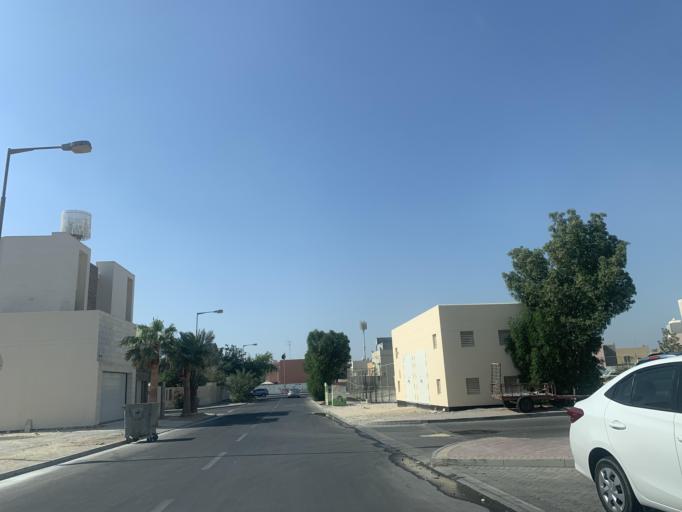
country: BH
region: Central Governorate
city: Madinat Hamad
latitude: 26.1219
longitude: 50.4949
